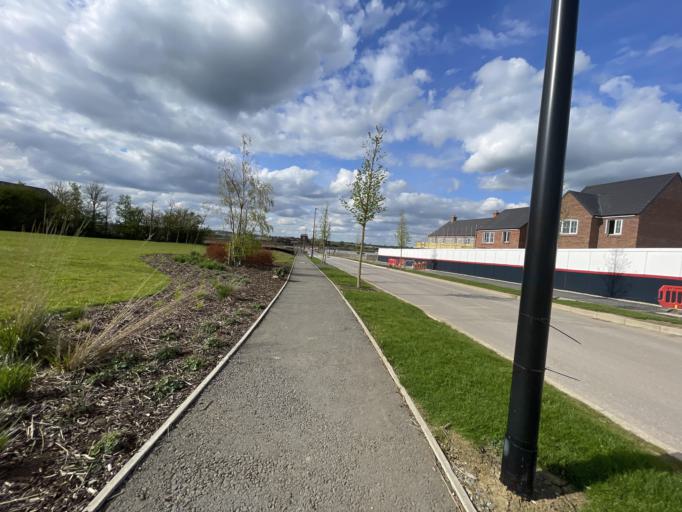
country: GB
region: England
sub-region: Warwickshire
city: Rugby
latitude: 52.3620
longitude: -1.1849
